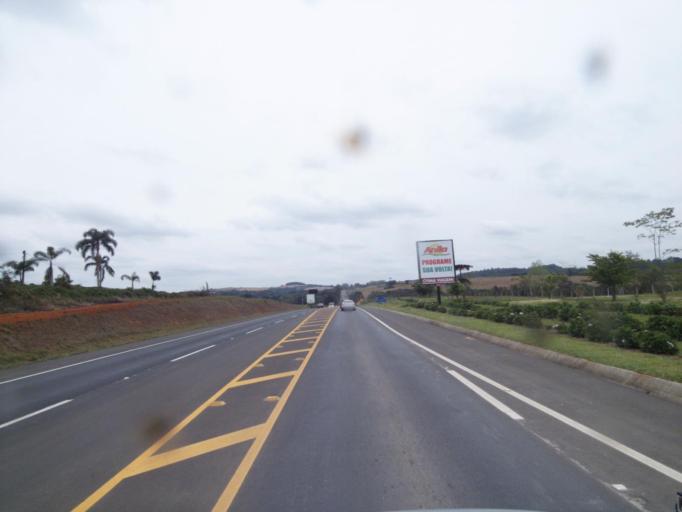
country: BR
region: Parana
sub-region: Irati
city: Irati
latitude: -25.4645
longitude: -50.5704
